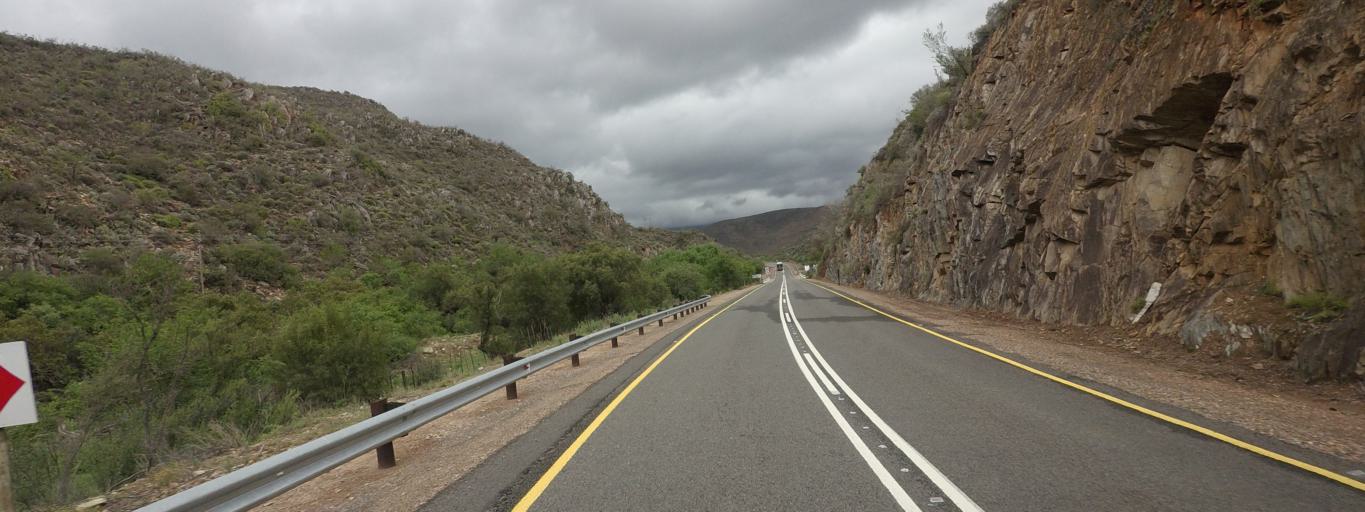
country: ZA
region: Western Cape
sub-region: Eden District Municipality
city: Oudtshoorn
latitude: -33.4216
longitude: 22.2414
